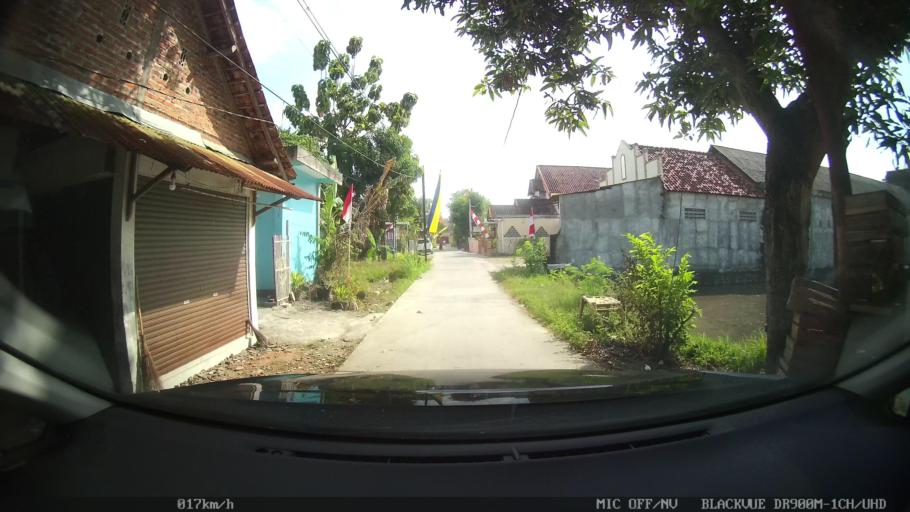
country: ID
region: Daerah Istimewa Yogyakarta
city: Kasihan
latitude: -7.8337
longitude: 110.3638
